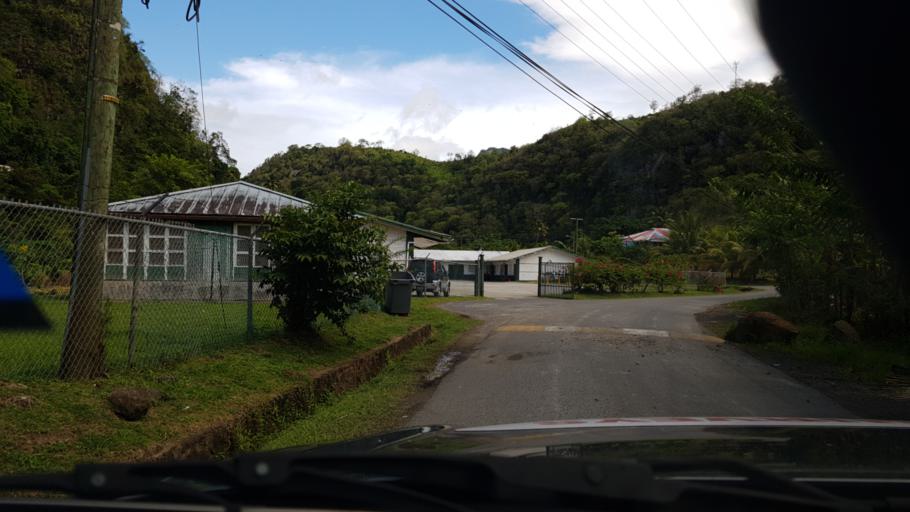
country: LC
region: Anse-la-Raye
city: Anse La Raye
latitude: 13.9379
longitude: -61.0409
